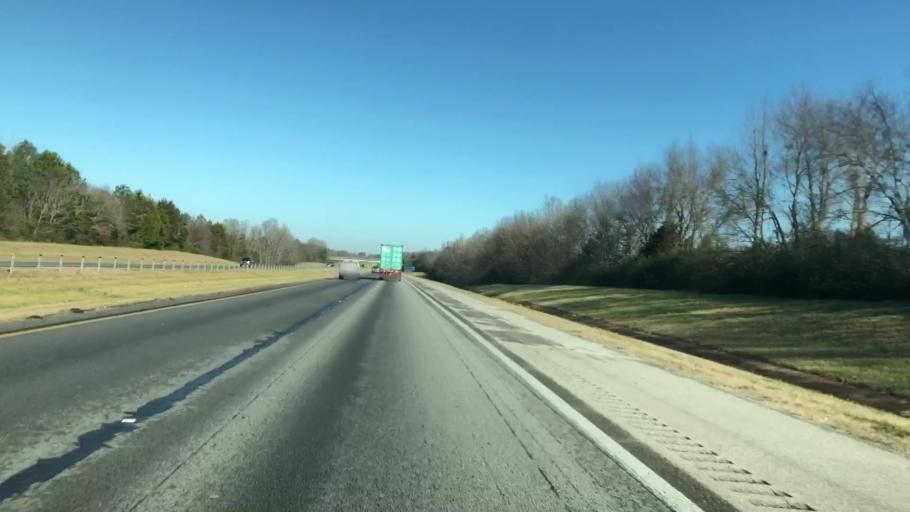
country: US
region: Alabama
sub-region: Limestone County
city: Athens
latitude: 34.8043
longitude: -86.9386
